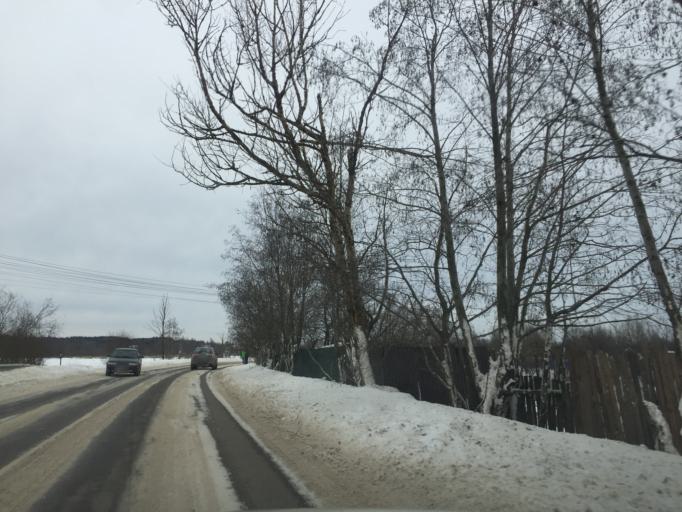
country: RU
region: Leningrad
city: Imeni Sverdlova
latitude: 59.7899
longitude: 30.7041
